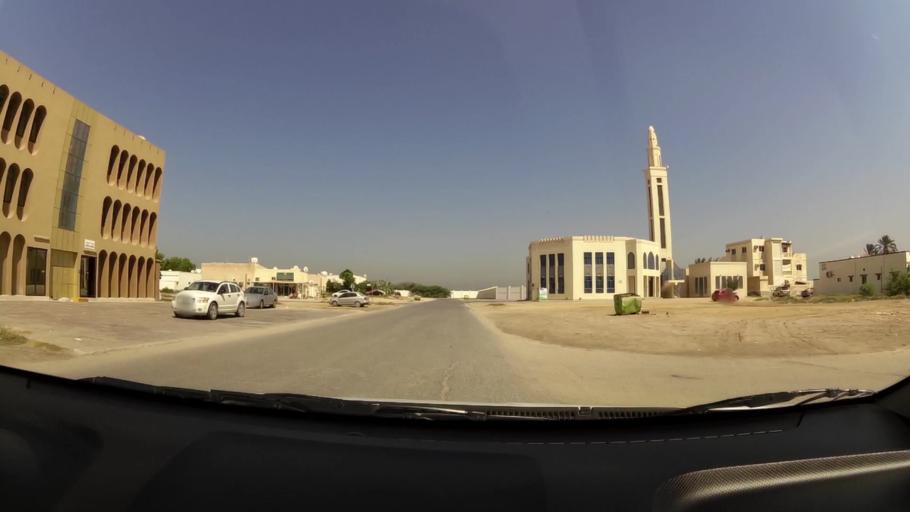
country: AE
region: Umm al Qaywayn
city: Umm al Qaywayn
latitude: 25.5813
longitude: 55.5596
